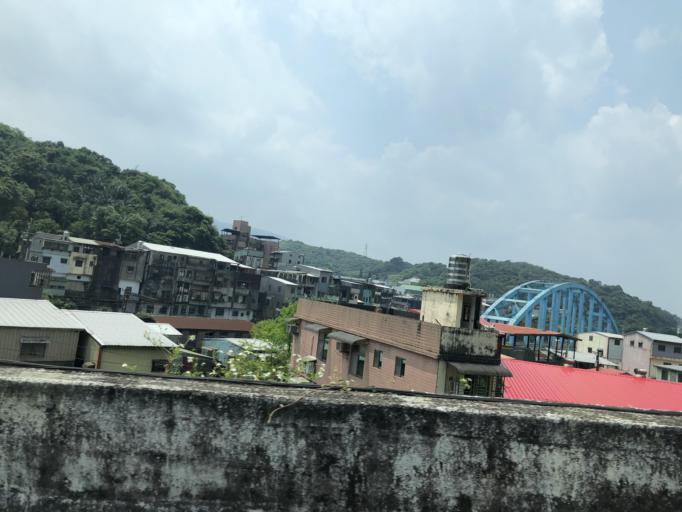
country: TW
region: Taiwan
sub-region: Keelung
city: Keelung
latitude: 25.1120
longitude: 121.7342
